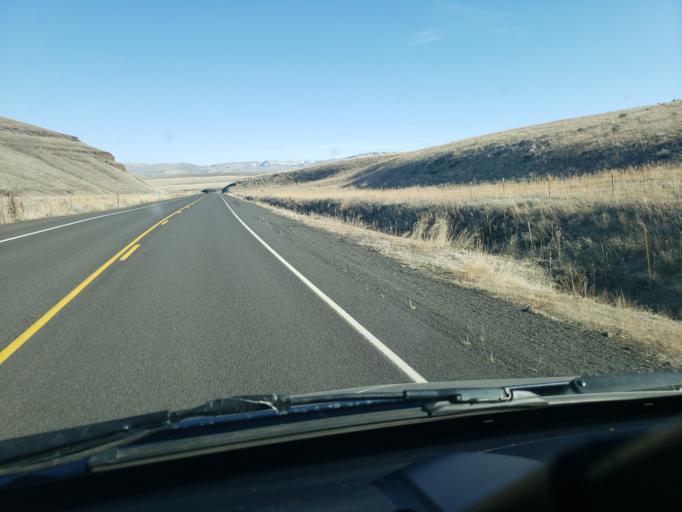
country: US
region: Oregon
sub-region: Umatilla County
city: Pilot Rock
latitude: 45.4666
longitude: -118.9114
